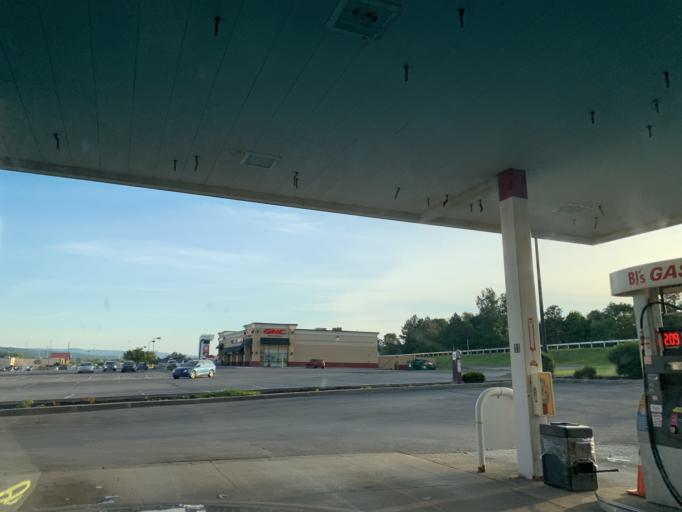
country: US
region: New York
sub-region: Oneida County
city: Utica
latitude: 43.1291
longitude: -75.2234
